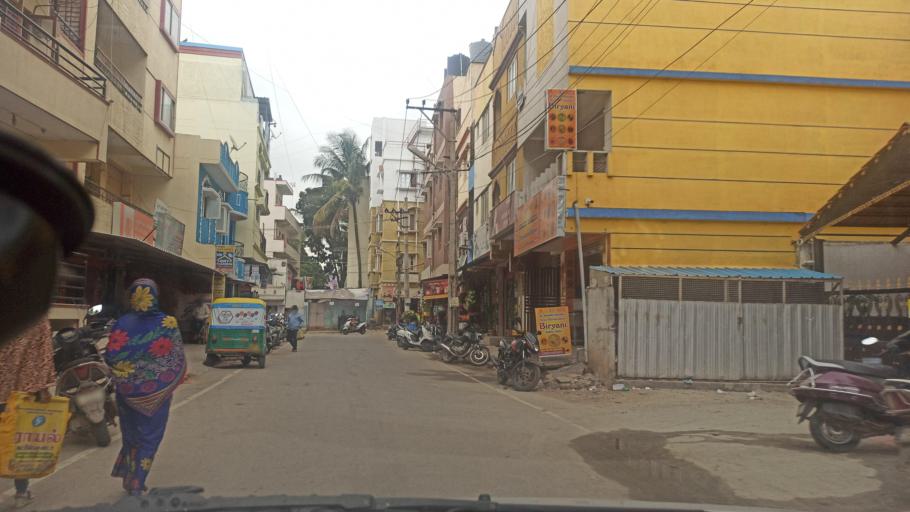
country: IN
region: Karnataka
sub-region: Bangalore Urban
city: Yelahanka
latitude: 13.0370
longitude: 77.6053
